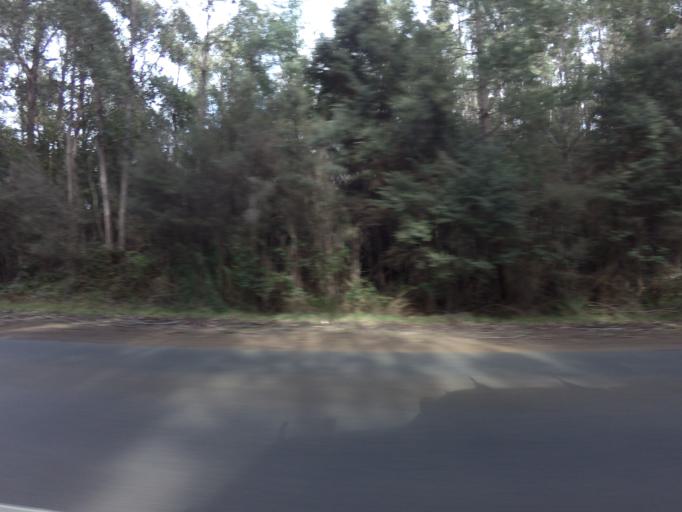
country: AU
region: Tasmania
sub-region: Huon Valley
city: Geeveston
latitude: -43.3532
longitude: 146.9572
